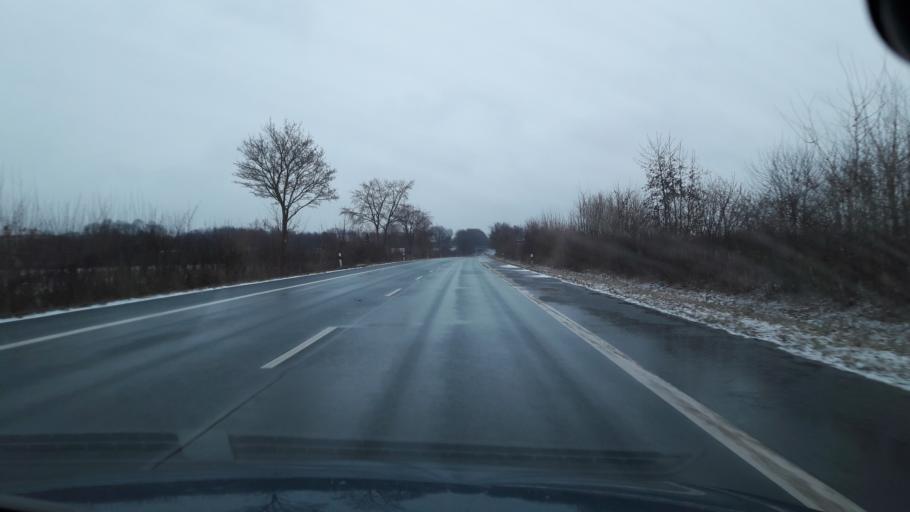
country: DE
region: North Rhine-Westphalia
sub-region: Regierungsbezirk Munster
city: Wadersloh
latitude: 51.7307
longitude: 8.2415
